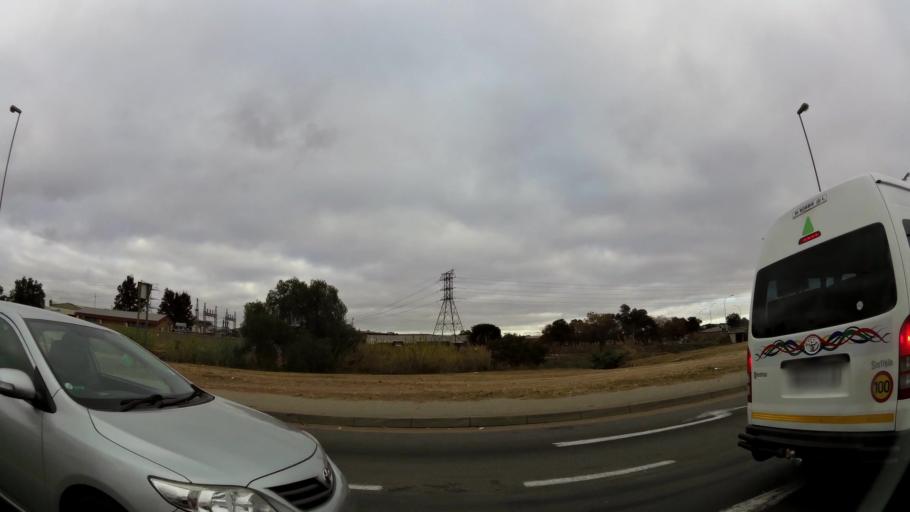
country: ZA
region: Limpopo
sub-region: Capricorn District Municipality
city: Polokwane
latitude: -23.9048
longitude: 29.4418
